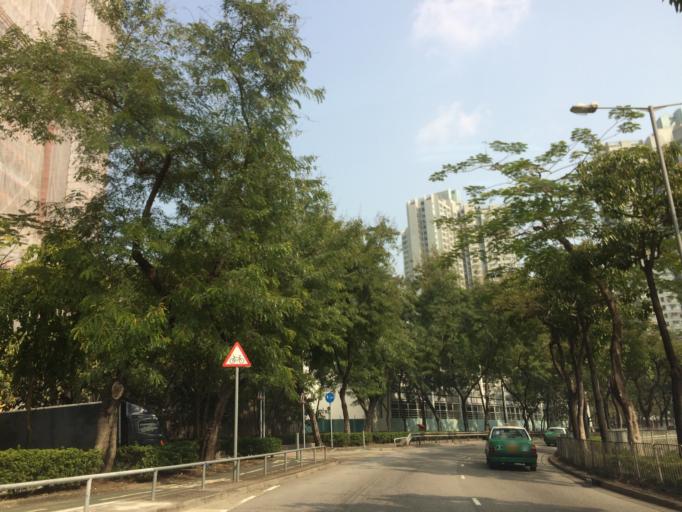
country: HK
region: Tai Po
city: Tai Po
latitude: 22.4569
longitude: 114.1680
